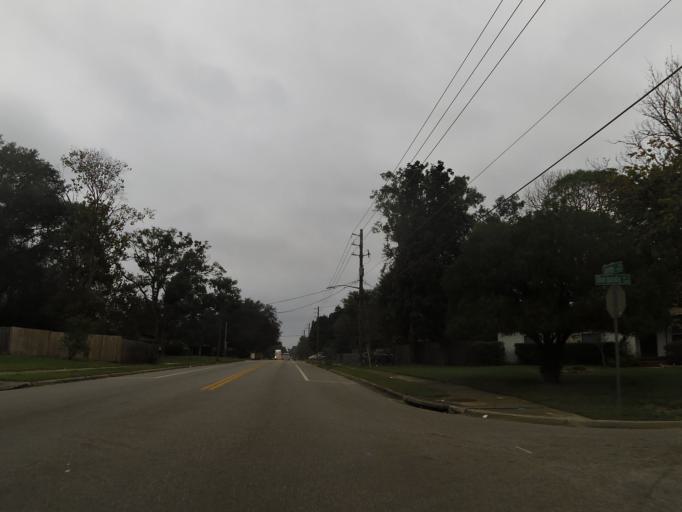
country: US
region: Florida
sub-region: Clay County
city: Bellair-Meadowbrook Terrace
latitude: 30.2542
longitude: -81.7473
